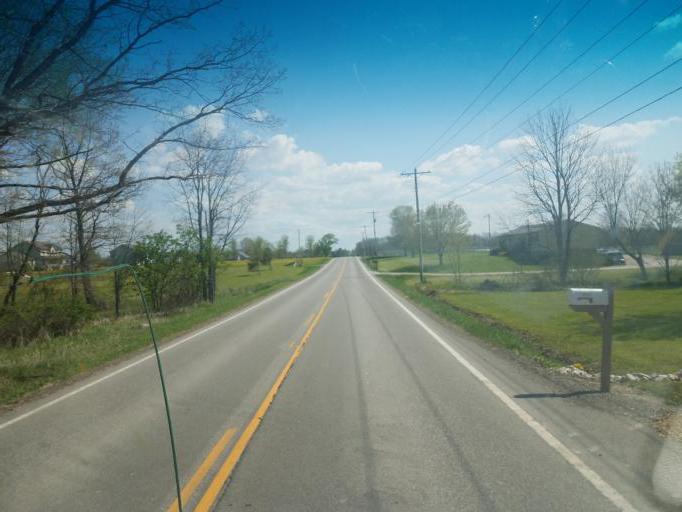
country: US
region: Ohio
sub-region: Wayne County
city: West Salem
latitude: 40.9285
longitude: -82.1092
